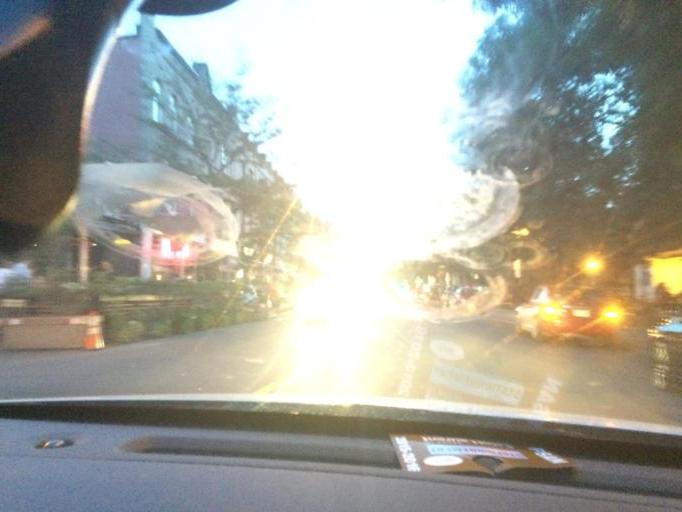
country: CA
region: Quebec
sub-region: Montreal
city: Montreal
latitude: 45.4890
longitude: -73.5681
